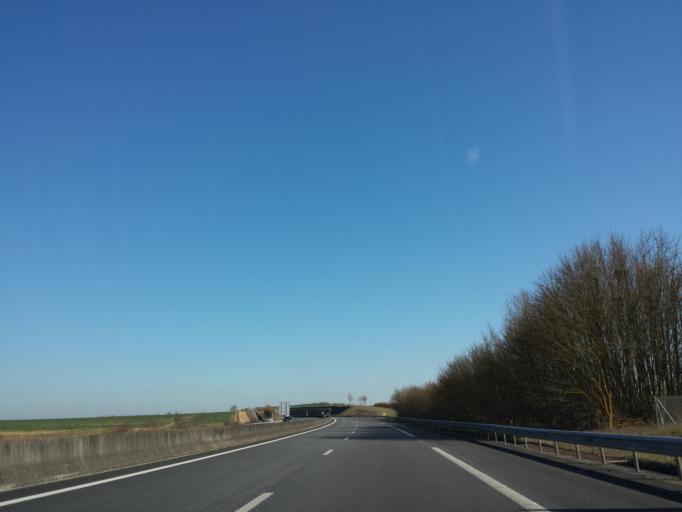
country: FR
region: Picardie
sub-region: Departement de l'Oise
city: Allonne
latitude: 49.4384
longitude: 2.1456
